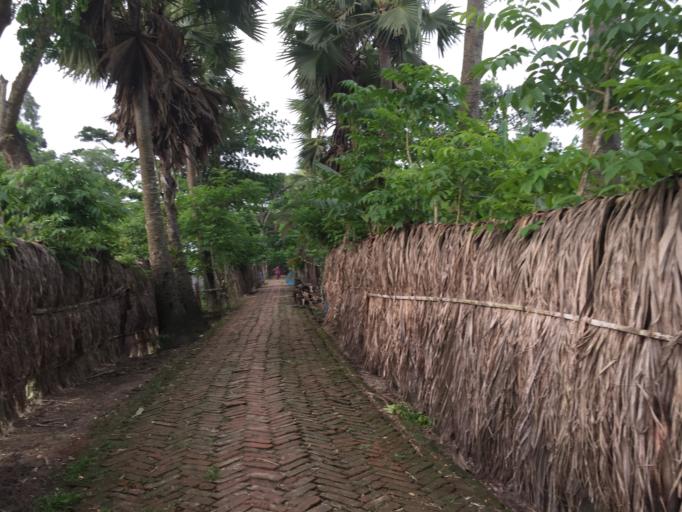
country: BD
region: Barisal
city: Mathba
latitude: 22.1902
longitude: 89.9297
